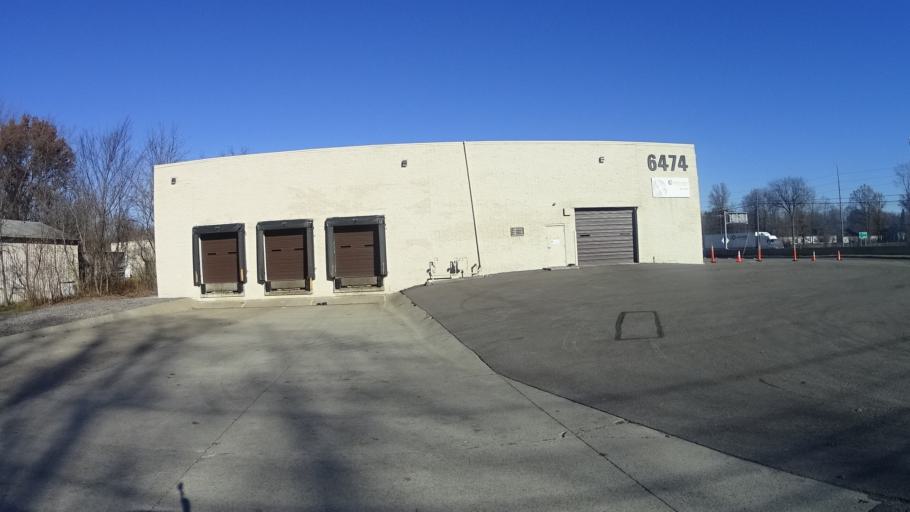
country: US
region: Ohio
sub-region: Lorain County
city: Sheffield
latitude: 41.4079
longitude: -82.1184
